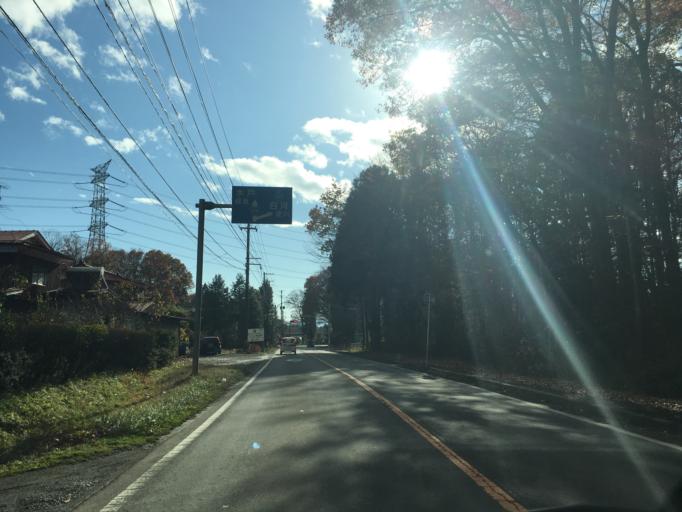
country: JP
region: Fukushima
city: Ishikawa
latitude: 37.0634
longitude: 140.3953
